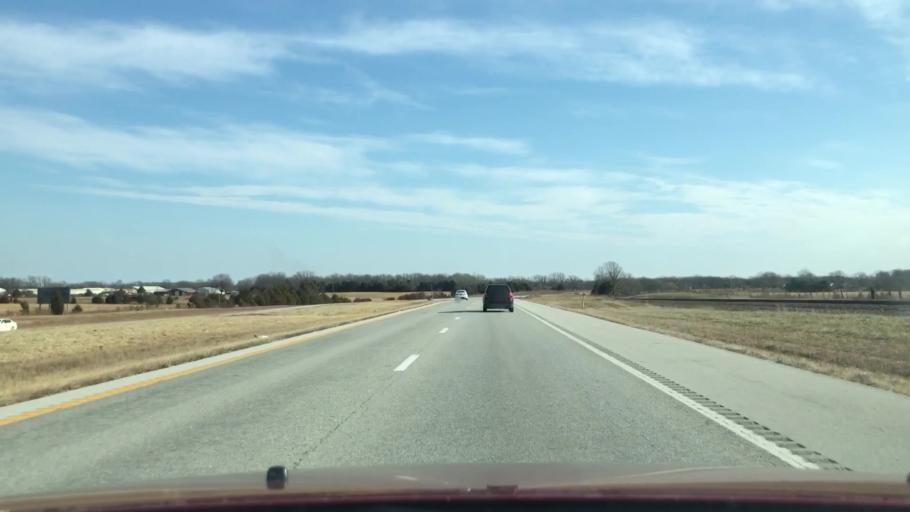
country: US
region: Missouri
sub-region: Webster County
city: Seymour
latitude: 37.1303
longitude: -92.7278
